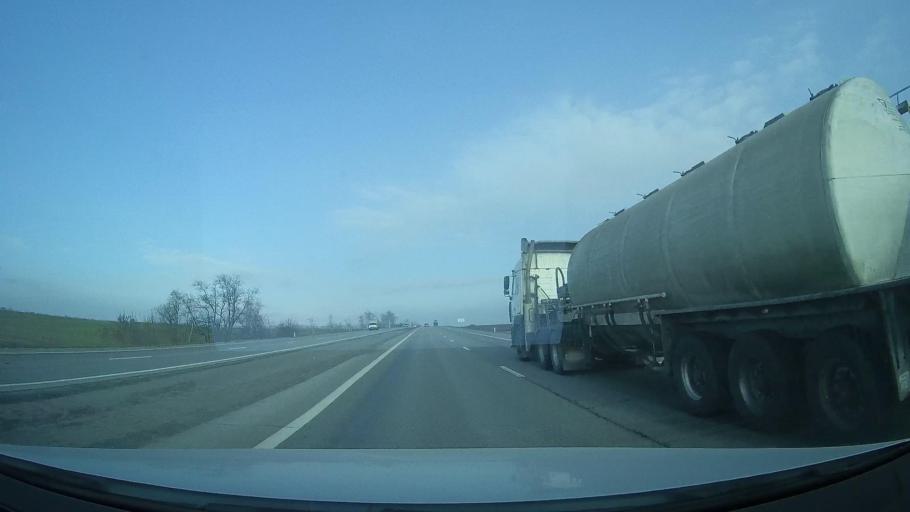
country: RU
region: Rostov
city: Grushevskaya
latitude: 47.4858
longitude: 39.9706
